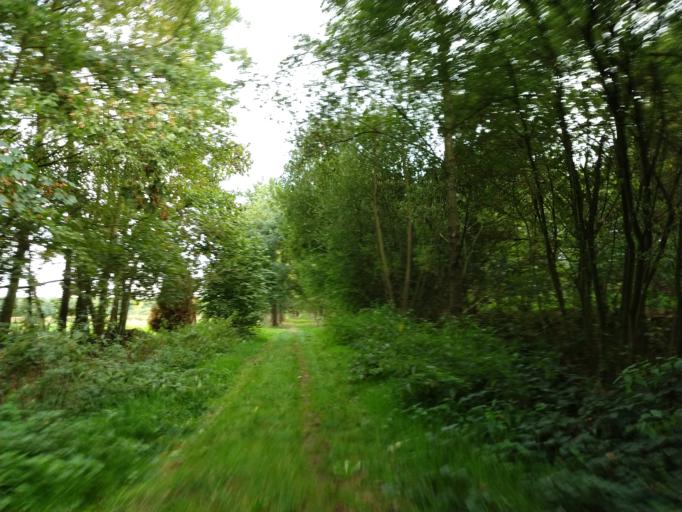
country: BE
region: Flanders
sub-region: Provincie Vlaams-Brabant
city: Haacht
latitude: 50.9808
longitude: 4.6554
